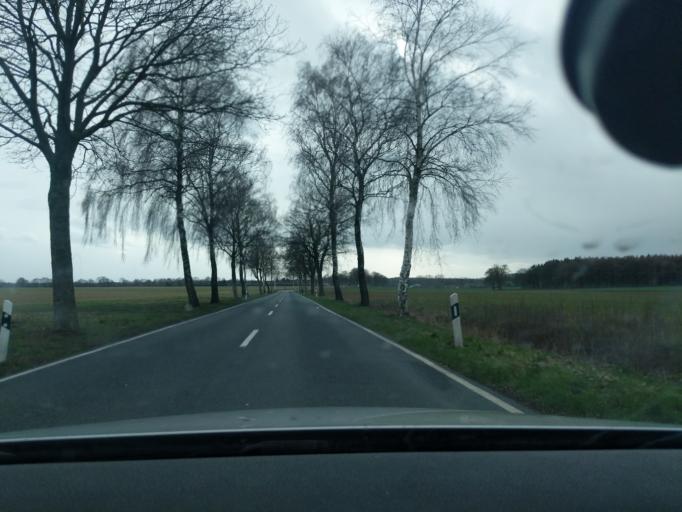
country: DE
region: Lower Saxony
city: Bliedersdorf
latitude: 53.4949
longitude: 9.5314
